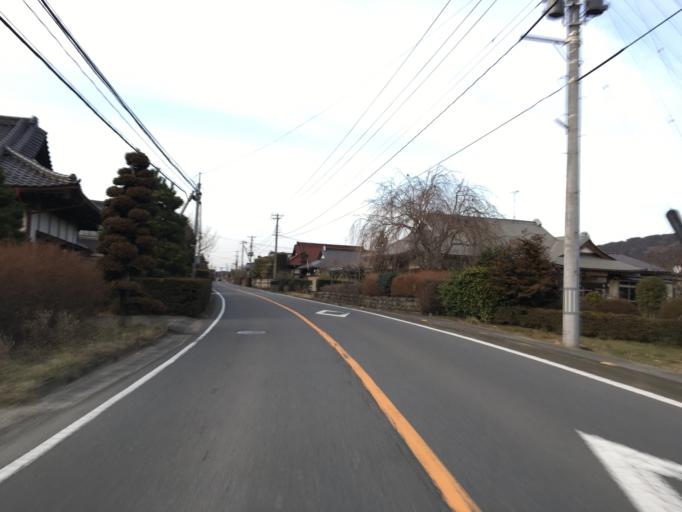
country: JP
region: Ibaraki
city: Daigo
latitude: 36.9295
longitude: 140.4089
